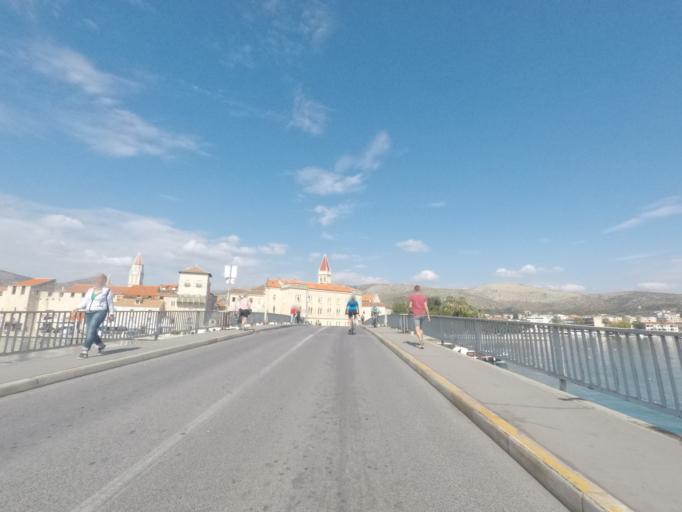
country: HR
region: Splitsko-Dalmatinska
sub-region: Grad Trogir
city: Trogir
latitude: 43.5153
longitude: 16.2522
